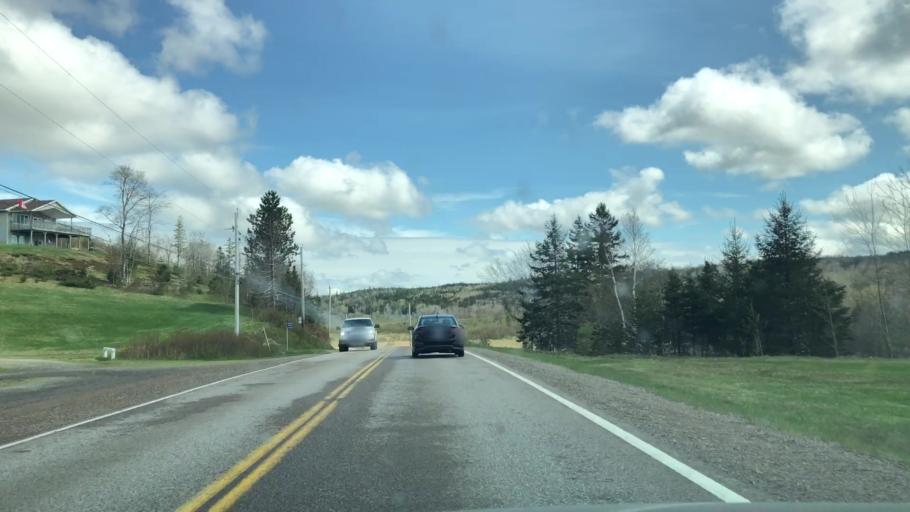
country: CA
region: Nova Scotia
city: Antigonish
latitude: 45.1978
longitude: -62.0022
